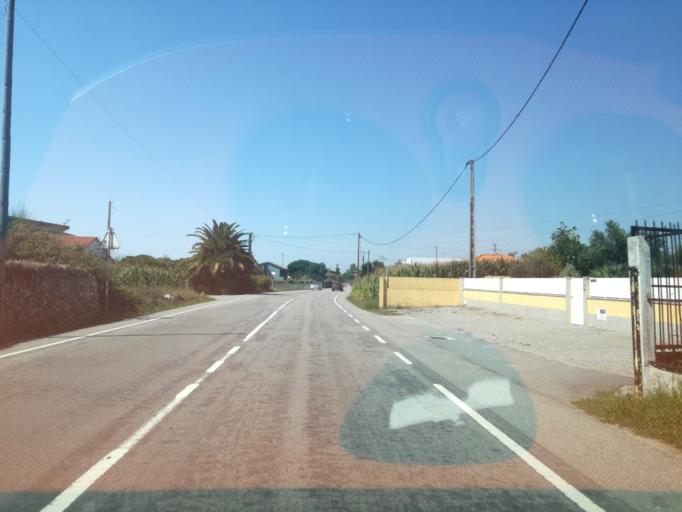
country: PT
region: Braga
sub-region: Esposende
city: Apulia
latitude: 41.4886
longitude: -8.7522
